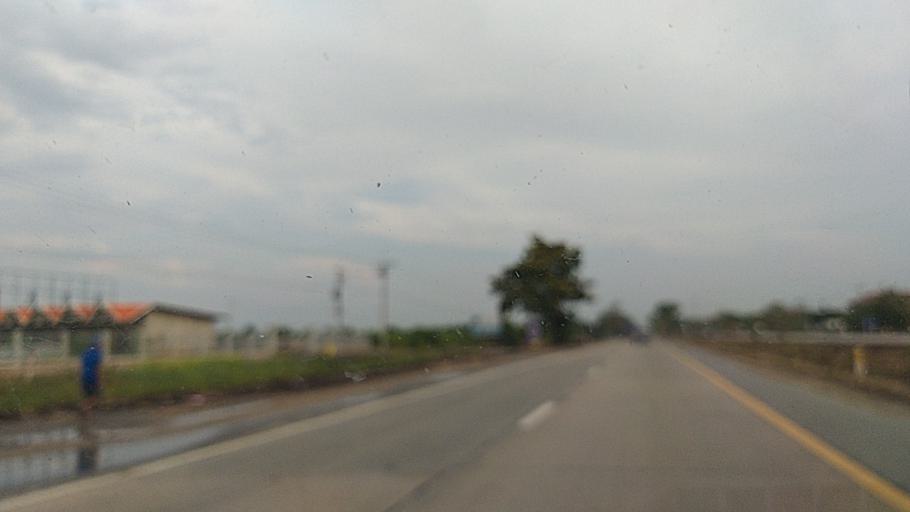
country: TH
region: Phra Nakhon Si Ayutthaya
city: Bang Pa-in
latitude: 14.2551
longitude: 100.5352
